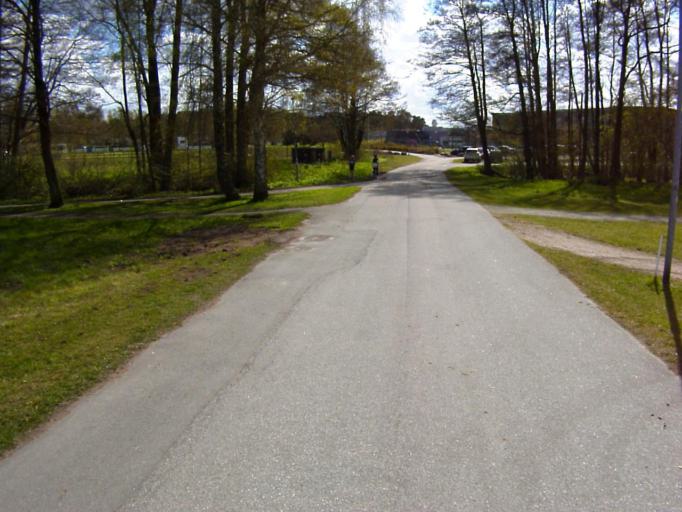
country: SE
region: Skane
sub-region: Kristianstads Kommun
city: Norra Asum
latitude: 56.0031
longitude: 14.0826
